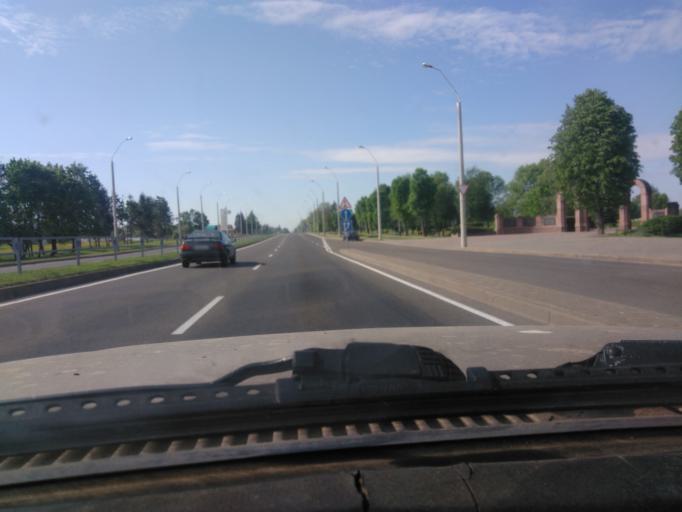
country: BY
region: Mogilev
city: Buynichy
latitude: 53.8619
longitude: 30.2582
